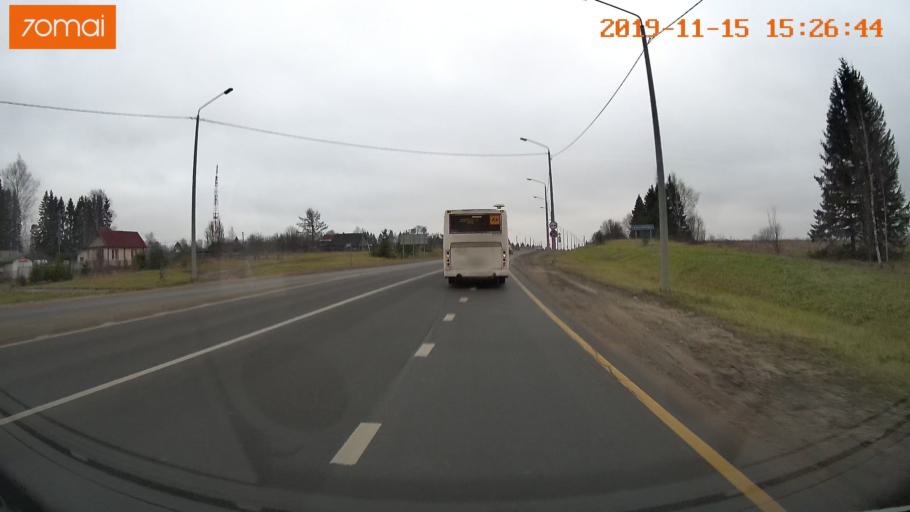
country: RU
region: Jaroslavl
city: Danilov
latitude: 58.1482
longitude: 40.1481
